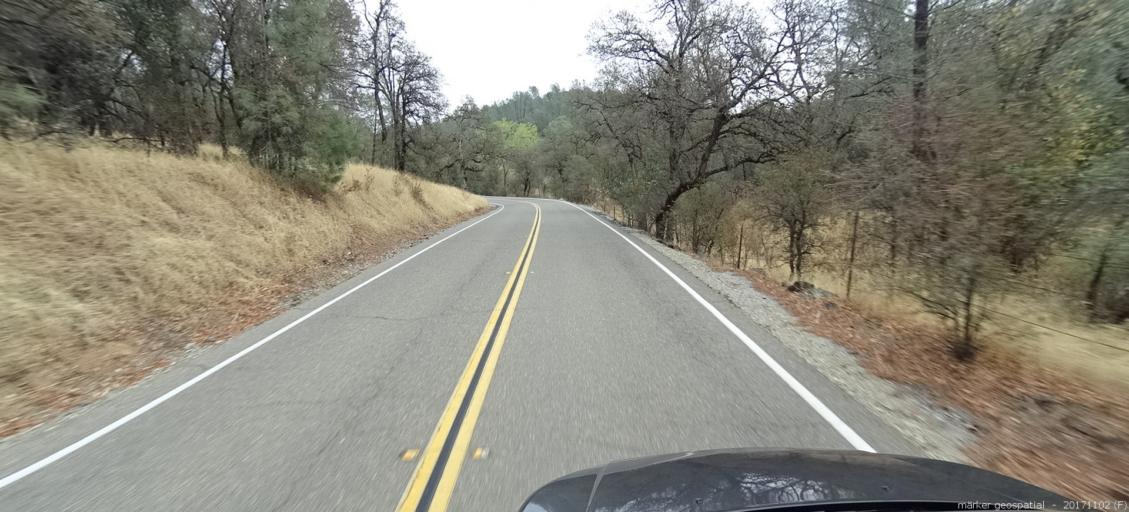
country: US
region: California
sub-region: Shasta County
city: Bella Vista
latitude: 40.7037
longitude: -122.2598
